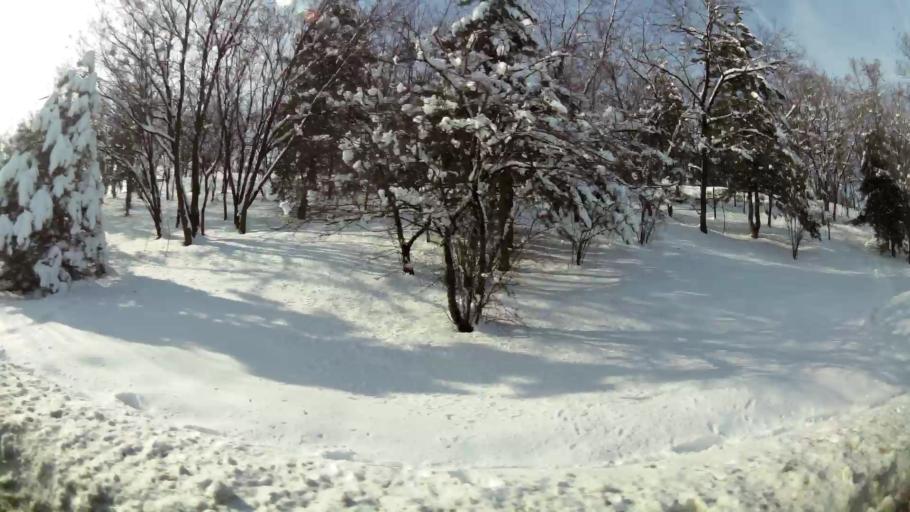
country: RS
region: Central Serbia
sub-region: Belgrade
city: Zvezdara
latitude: 44.7873
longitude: 20.5276
